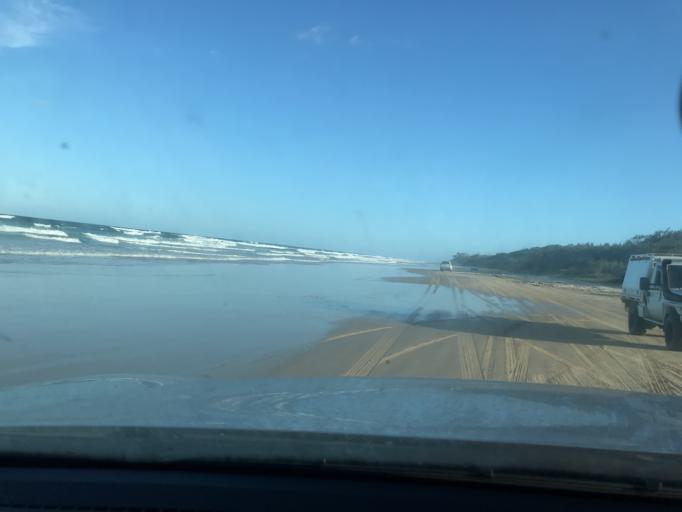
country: AU
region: Queensland
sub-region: Fraser Coast
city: Urangan
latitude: -25.4111
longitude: 153.1703
